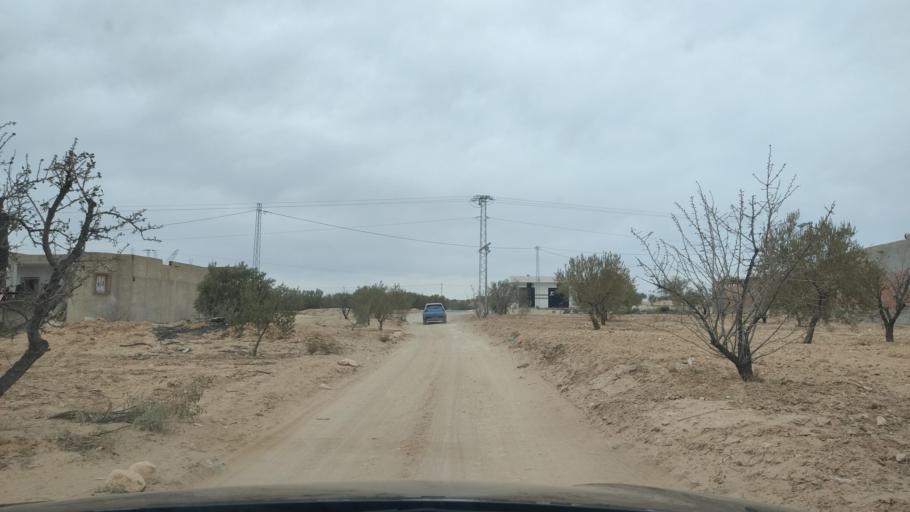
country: TN
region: Al Qasrayn
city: Kasserine
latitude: 35.2303
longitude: 8.9104
